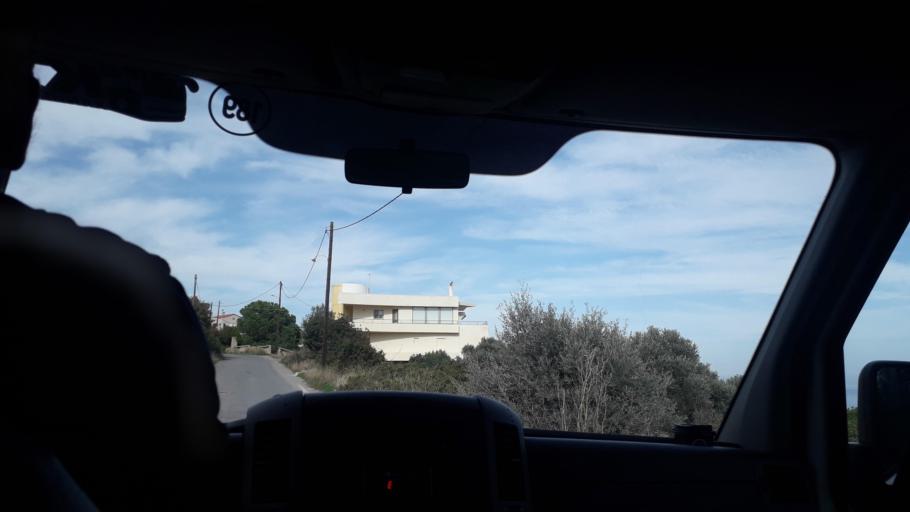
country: GR
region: Crete
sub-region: Nomos Rethymnis
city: Atsipopoulon
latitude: 35.3627
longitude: 24.4381
